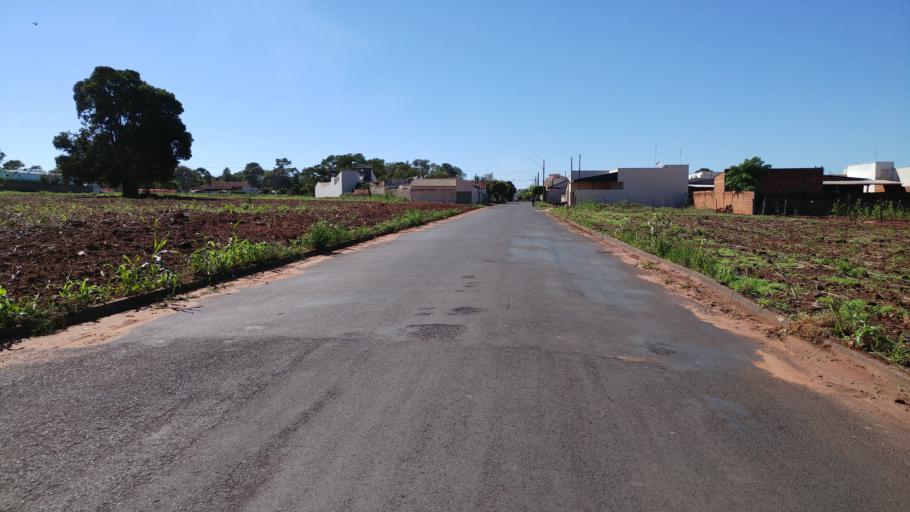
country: BR
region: Sao Paulo
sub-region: Paraguacu Paulista
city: Paraguacu Paulista
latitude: -22.4182
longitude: -50.5867
